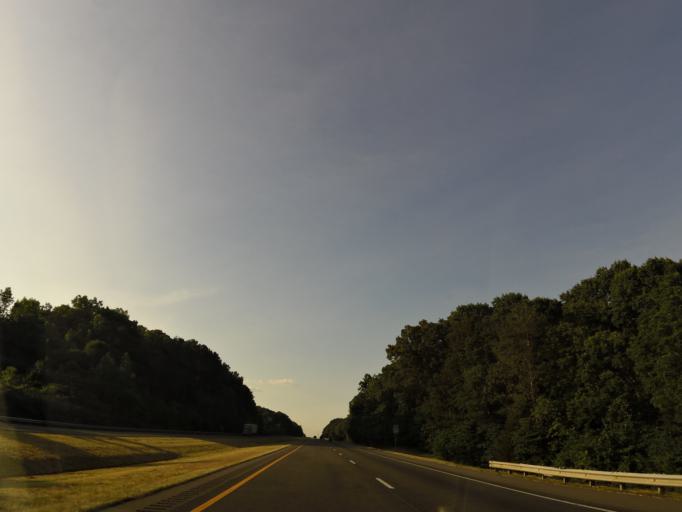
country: US
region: Alabama
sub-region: DeKalb County
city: Fort Payne
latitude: 34.5125
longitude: -85.6921
